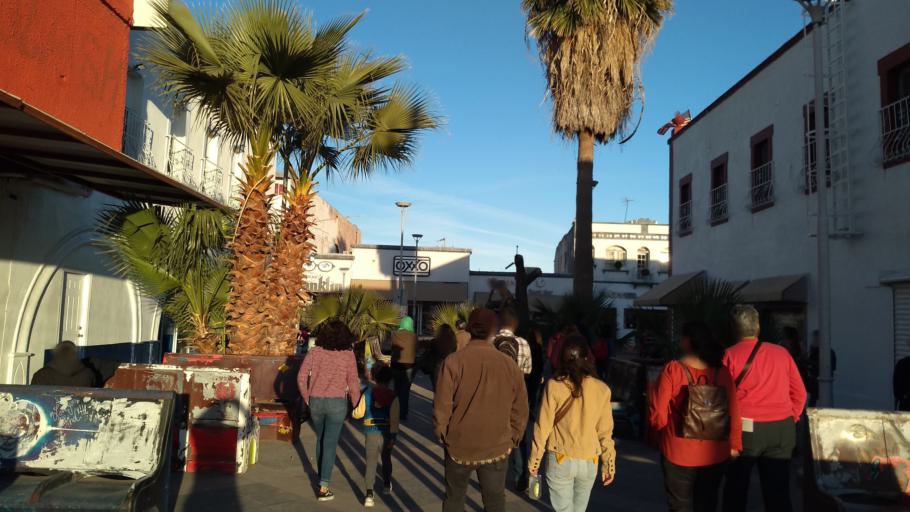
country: MX
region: Chihuahua
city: Ciudad Juarez
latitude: 31.7432
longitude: -106.4861
